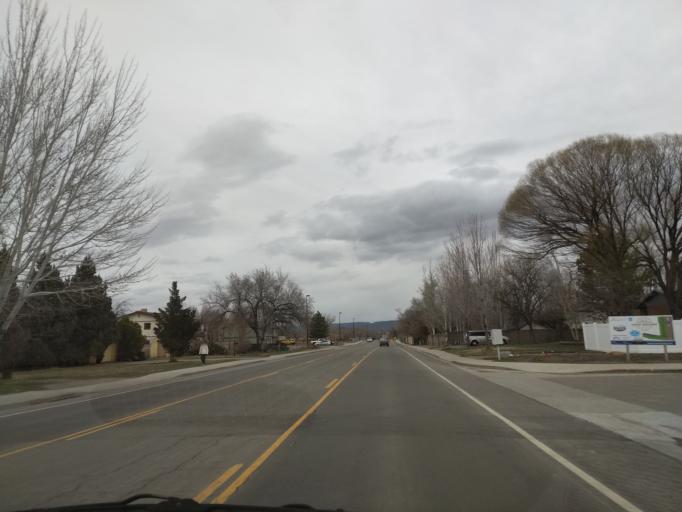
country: US
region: Colorado
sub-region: Mesa County
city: Fruitvale
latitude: 39.0885
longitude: -108.5152
